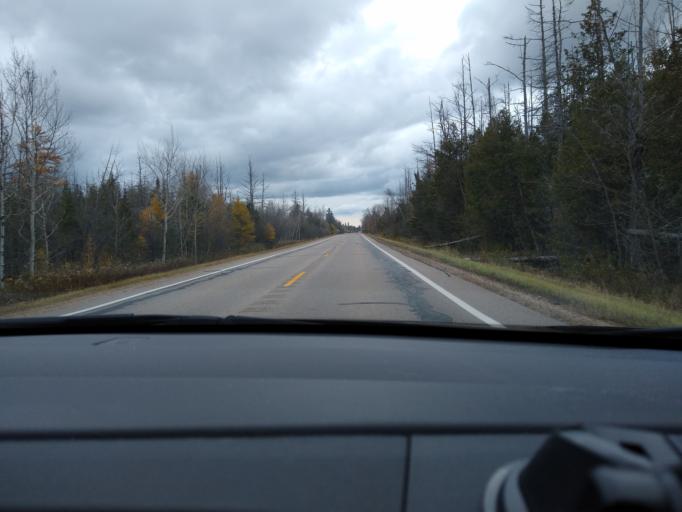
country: US
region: Michigan
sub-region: Delta County
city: Escanaba
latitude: 45.7310
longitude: -87.2638
